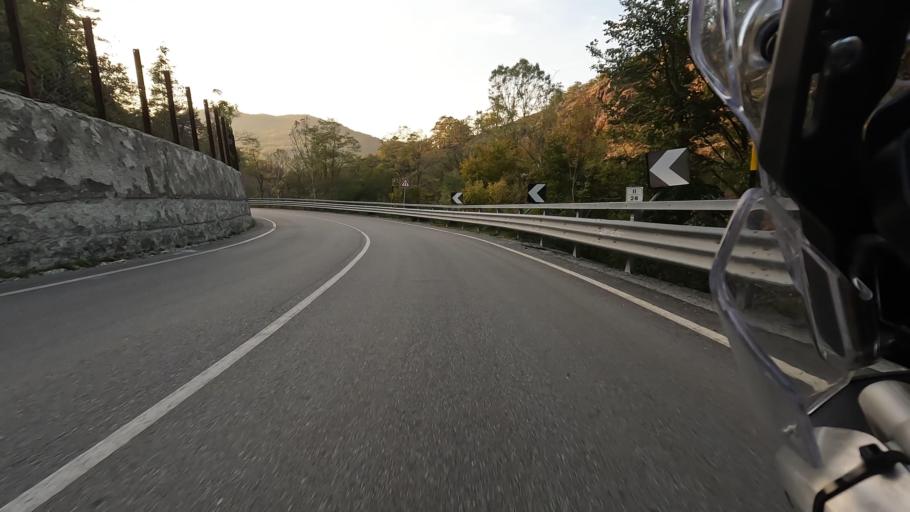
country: IT
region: Liguria
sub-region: Provincia di Savona
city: Sassello
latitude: 44.5193
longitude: 8.4734
